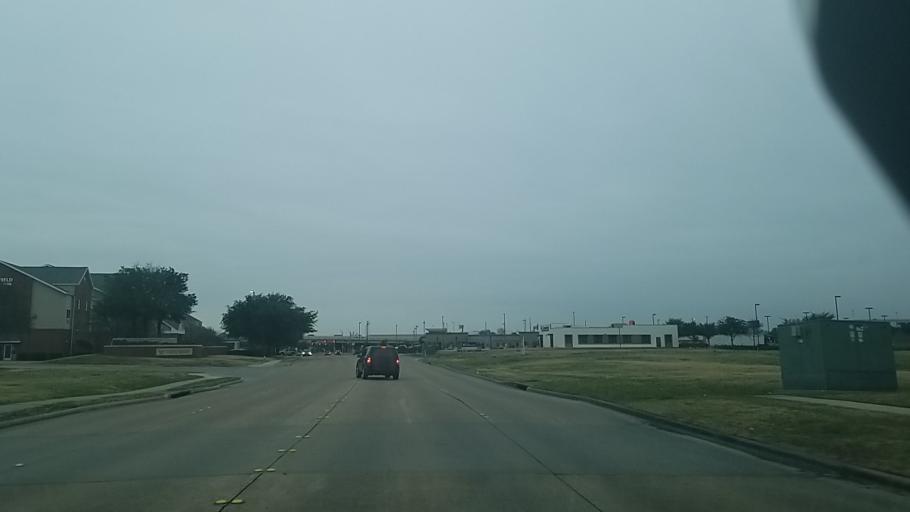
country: US
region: Texas
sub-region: Denton County
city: Lewisville
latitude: 32.9980
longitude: -96.9672
